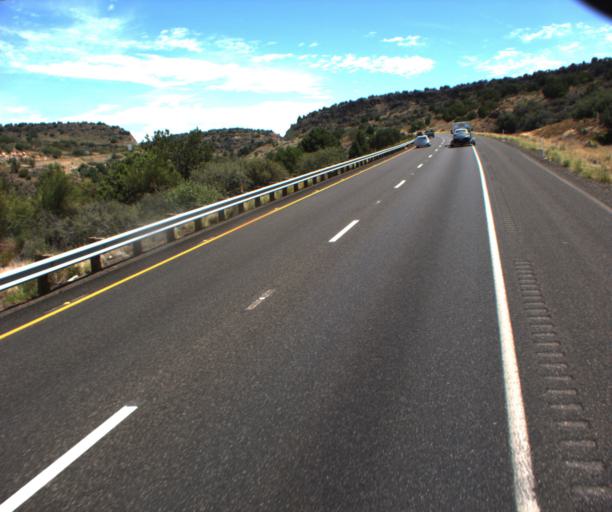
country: US
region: Arizona
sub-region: Yavapai County
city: Big Park
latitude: 34.7085
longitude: -111.7320
